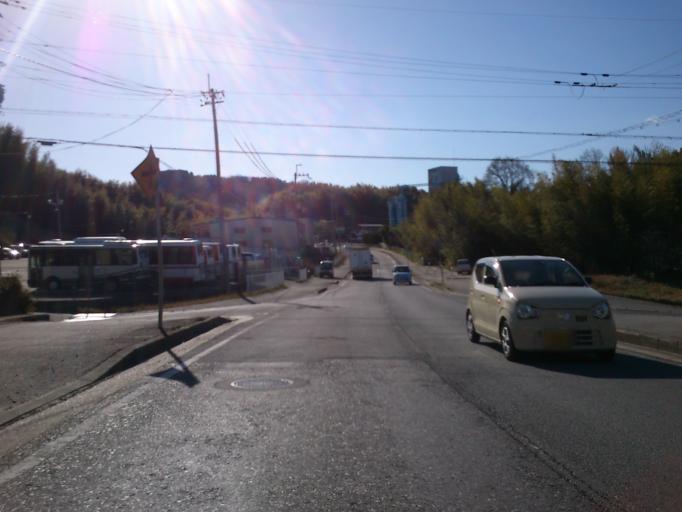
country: JP
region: Kyoto
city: Tanabe
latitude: 34.8120
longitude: 135.7571
